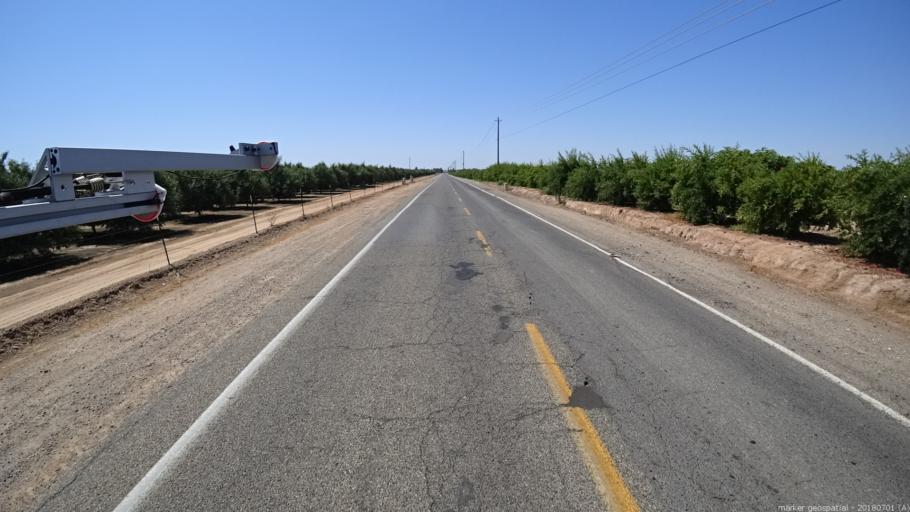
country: US
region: California
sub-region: Madera County
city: Madera Acres
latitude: 37.0025
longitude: -120.0287
